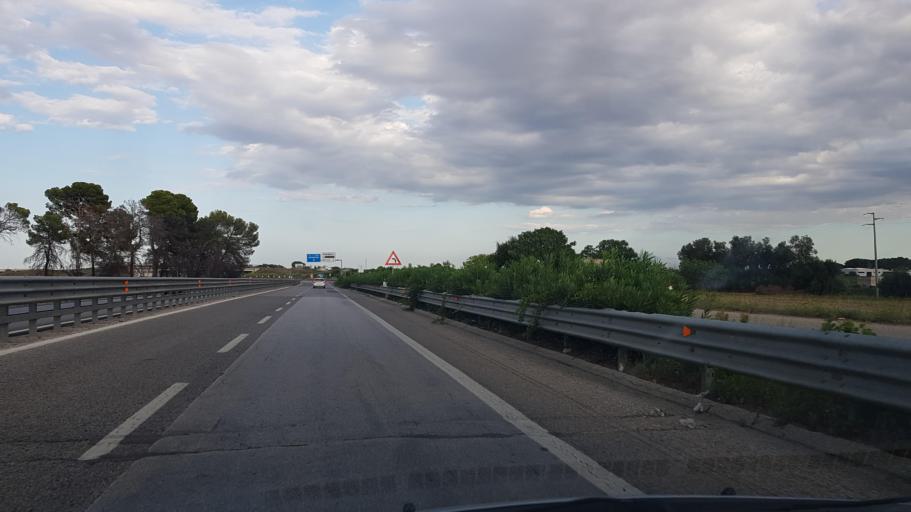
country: IT
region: Apulia
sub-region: Provincia di Brindisi
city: Francavilla Fontana
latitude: 40.5333
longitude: 17.5218
